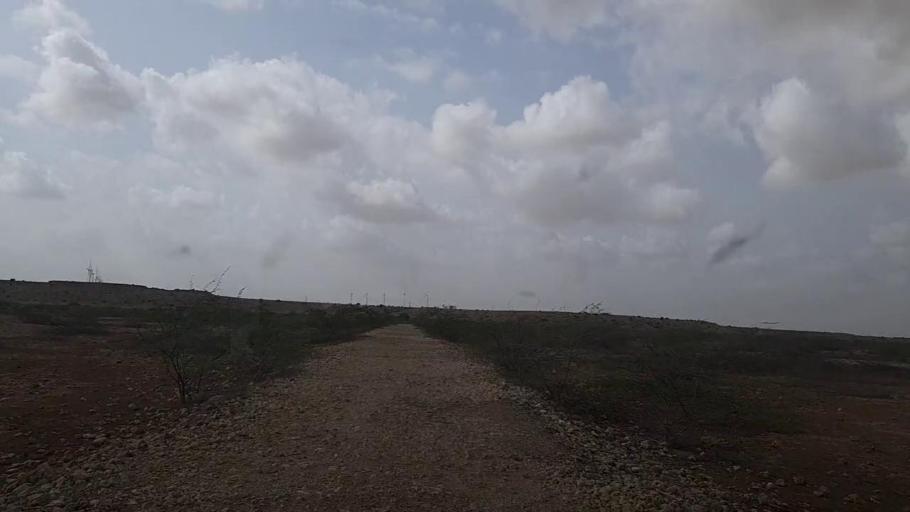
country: PK
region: Sindh
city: Thatta
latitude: 24.9230
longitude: 67.8934
